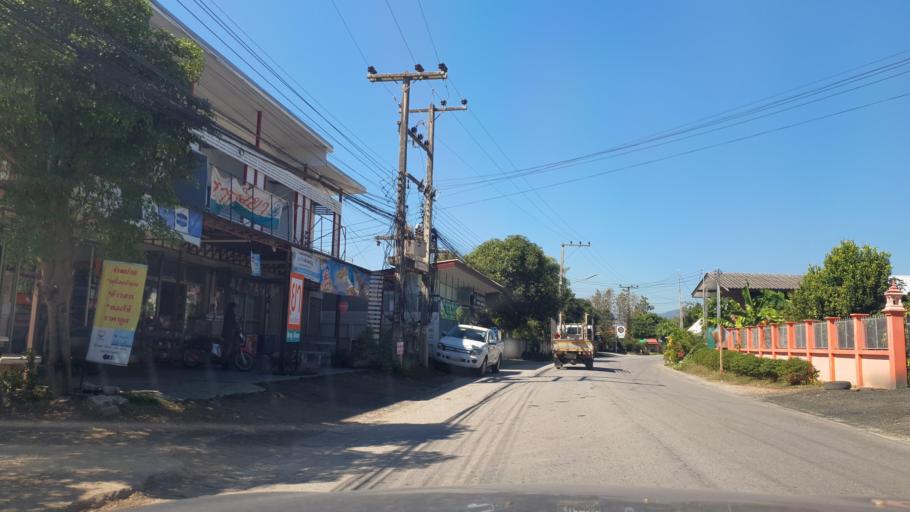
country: TH
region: Chiang Mai
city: San Pa Tong
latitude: 18.6425
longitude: 98.8451
